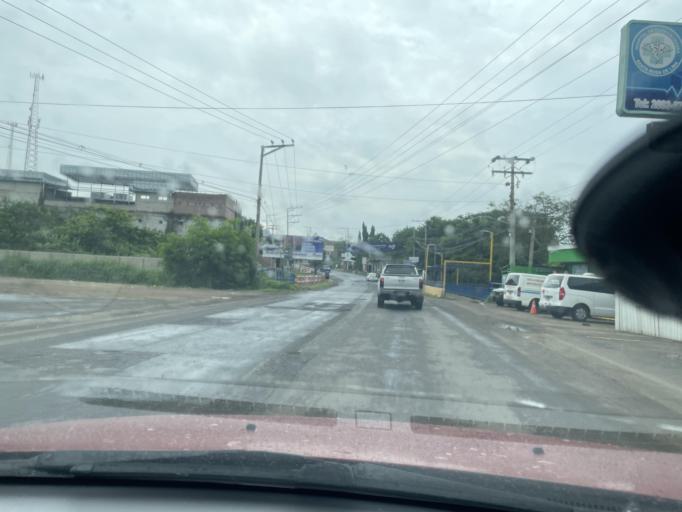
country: SV
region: La Union
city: Santa Rosa de Lima
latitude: 13.6229
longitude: -87.8945
